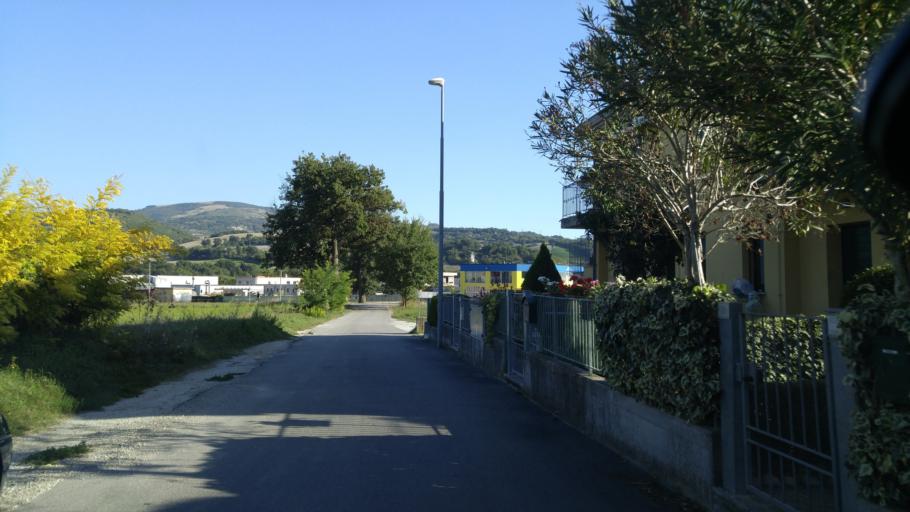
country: IT
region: The Marches
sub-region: Provincia di Pesaro e Urbino
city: Fermignano
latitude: 43.6903
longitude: 12.6456
